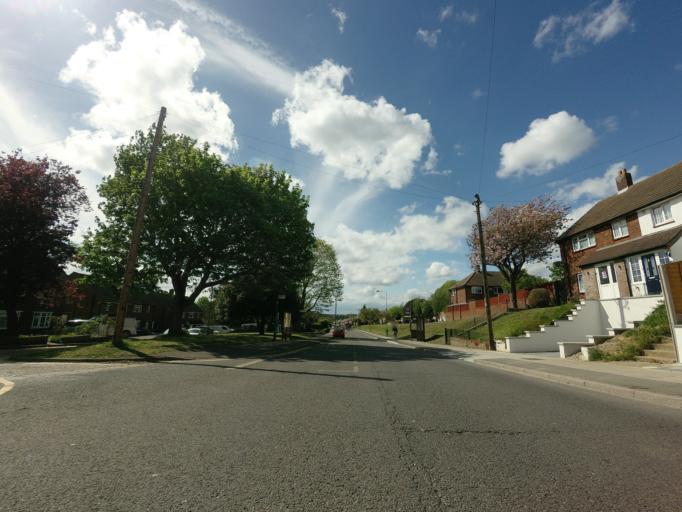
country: GB
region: England
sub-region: Greater London
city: Orpington
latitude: 51.3771
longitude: 0.1201
